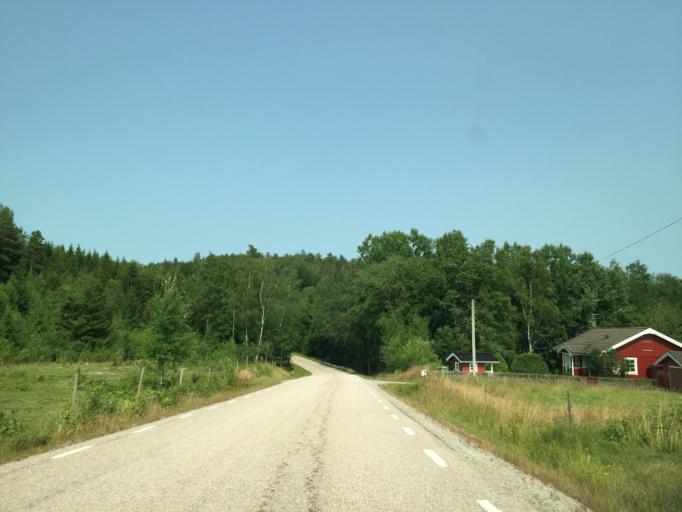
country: SE
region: Vaestra Goetaland
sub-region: Lilla Edets Kommun
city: Lilla Edet
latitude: 58.1669
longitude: 12.0758
